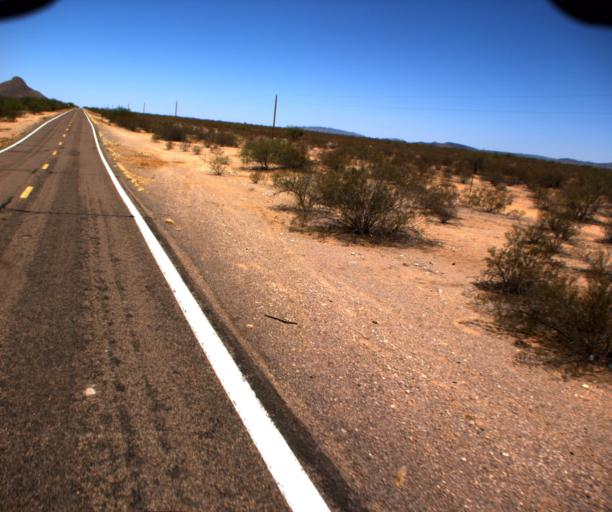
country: US
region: Arizona
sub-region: Pima County
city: Ajo
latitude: 32.2001
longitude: -112.4938
